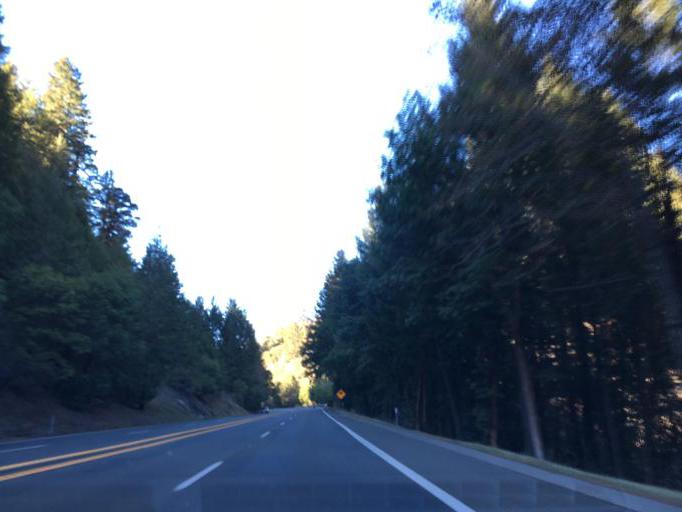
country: US
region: California
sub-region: Mendocino County
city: Laytonville
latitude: 39.6058
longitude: -123.4556
